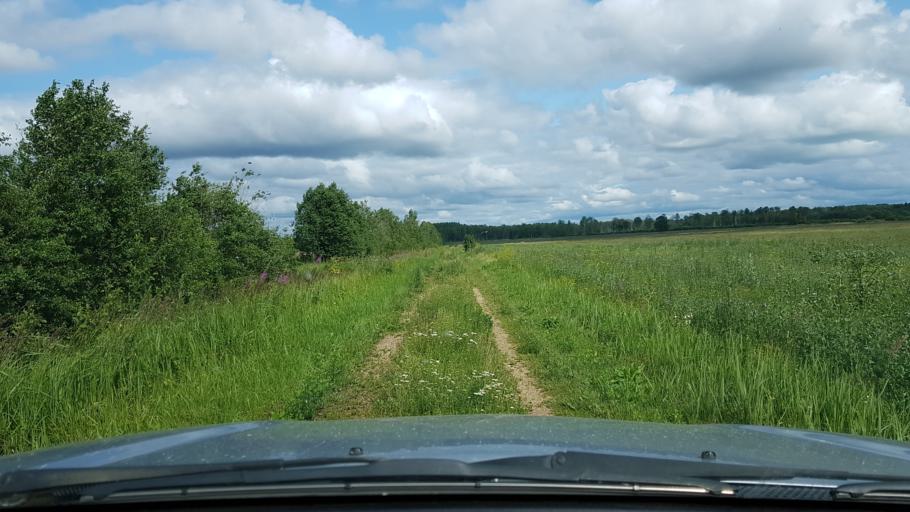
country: EE
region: Ida-Virumaa
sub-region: Narva-Joesuu linn
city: Narva-Joesuu
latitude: 59.3832
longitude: 27.9375
